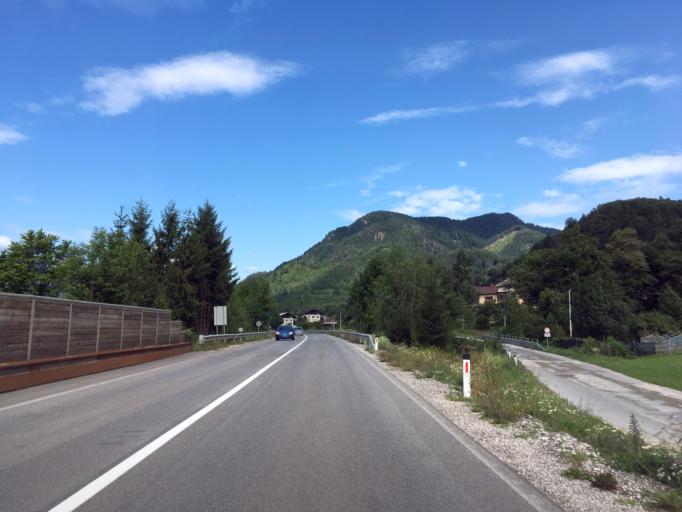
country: SI
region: Jesenice
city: Slovenski Javornik
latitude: 46.4237
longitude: 14.1012
